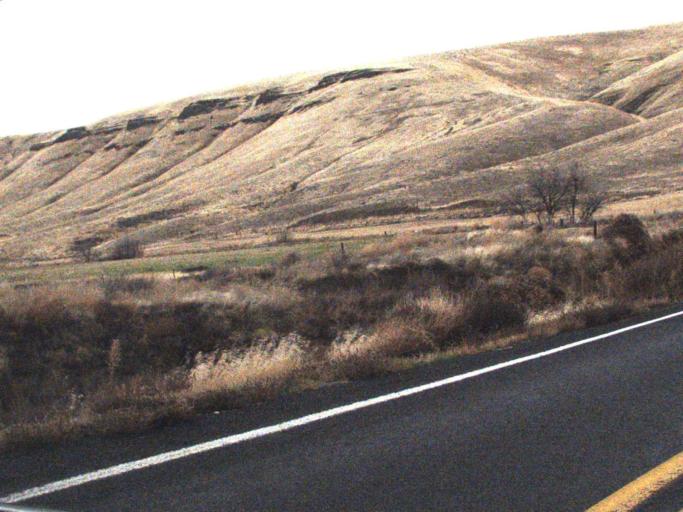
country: US
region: Washington
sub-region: Columbia County
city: Dayton
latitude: 46.5112
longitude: -117.9728
